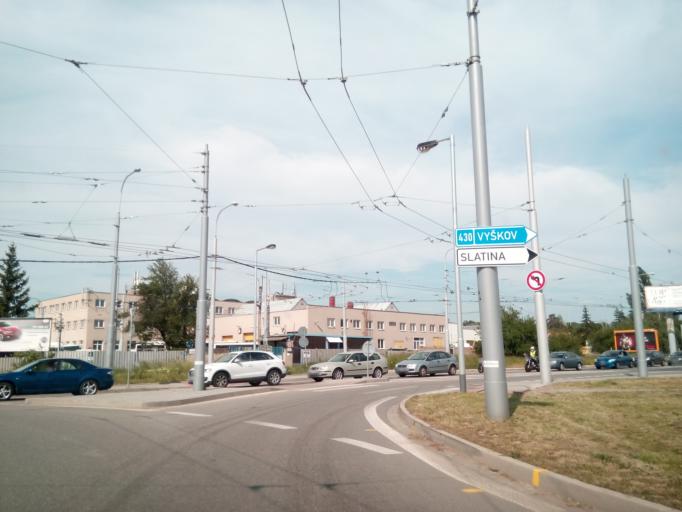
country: CZ
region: South Moravian
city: Podoli
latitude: 49.1831
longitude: 16.6682
